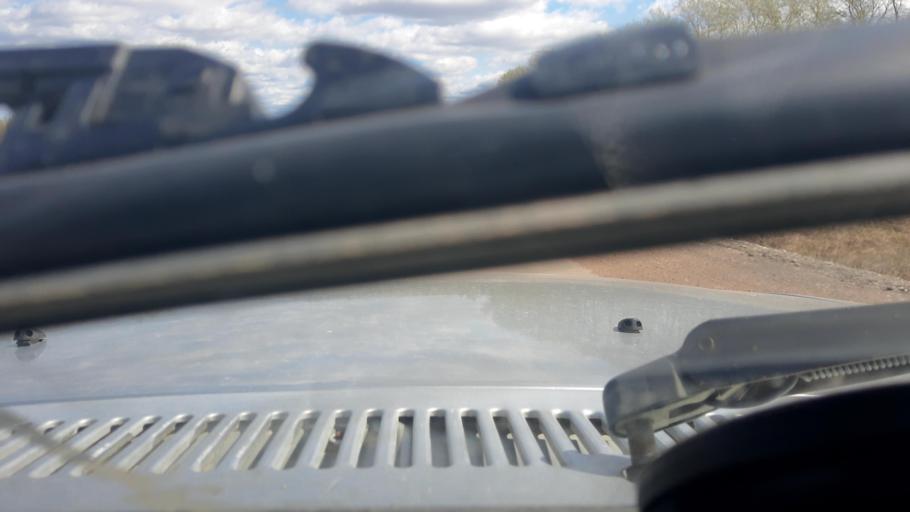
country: RU
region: Bashkortostan
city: Yazykovo
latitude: 55.2737
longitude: 56.2712
